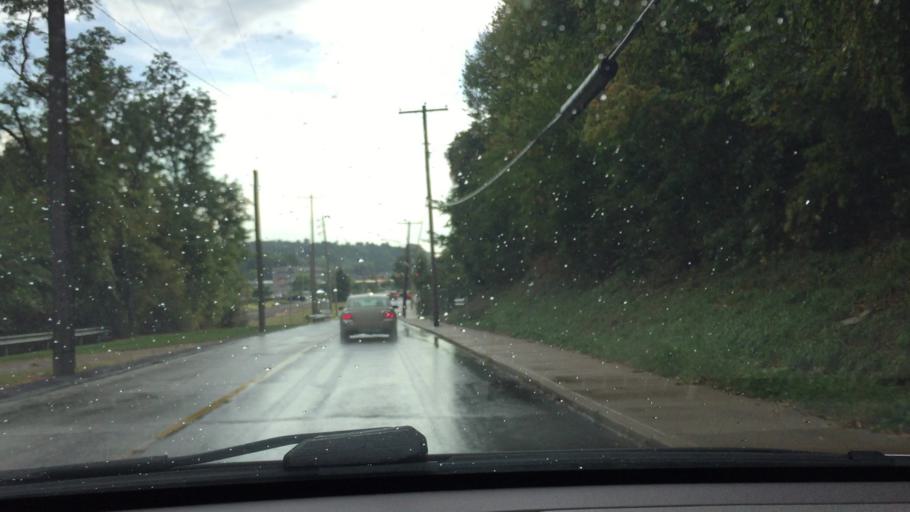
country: US
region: Pennsylvania
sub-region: Washington County
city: Canonsburg
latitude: 40.2641
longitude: -80.1749
